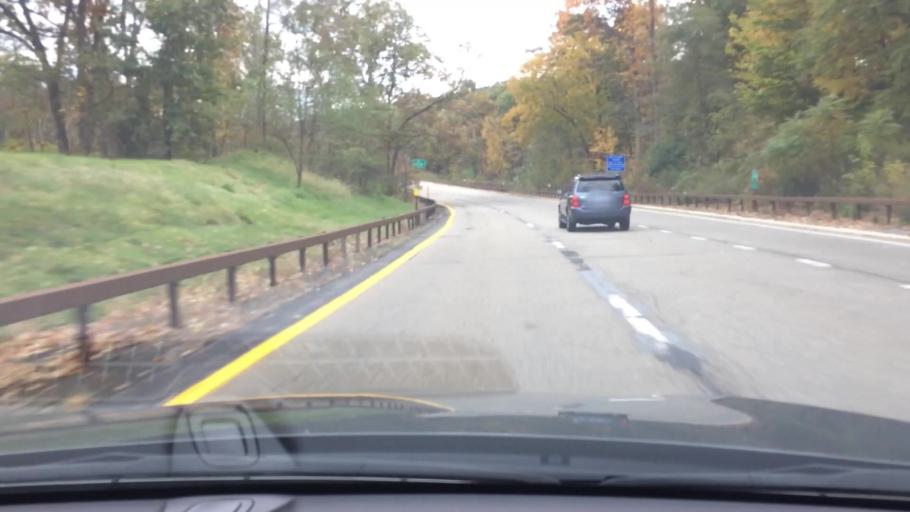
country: US
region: New York
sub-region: Dutchess County
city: Hillside Lake
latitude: 41.6311
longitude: -73.7817
